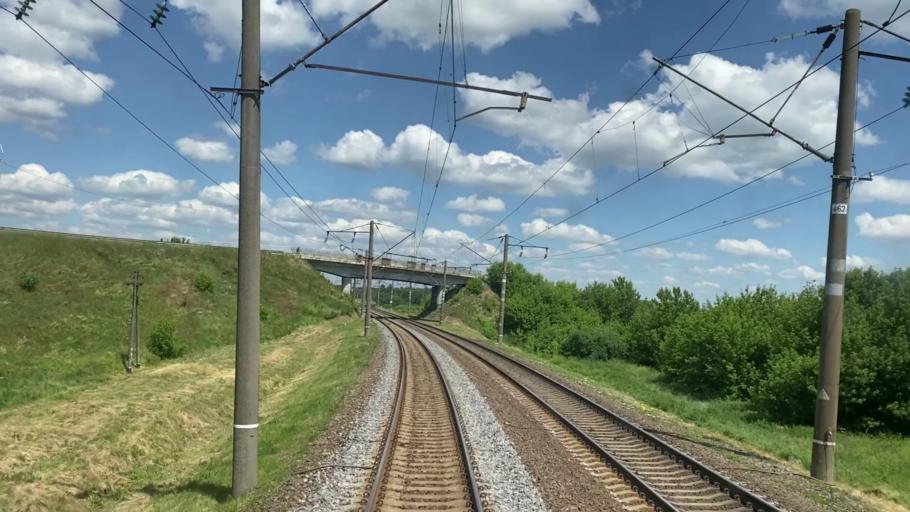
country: BY
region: Brest
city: Ivatsevichy
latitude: 52.7179
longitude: 25.3575
